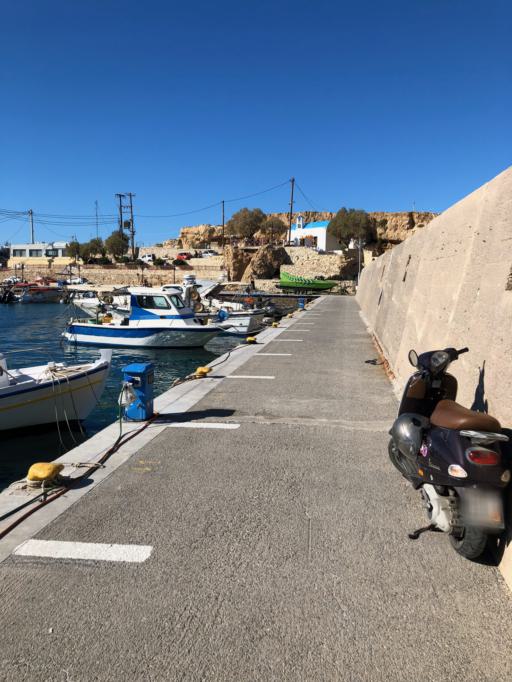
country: GR
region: Crete
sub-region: Nomos Irakleiou
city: Limin Khersonisou
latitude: 35.3223
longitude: 25.3928
